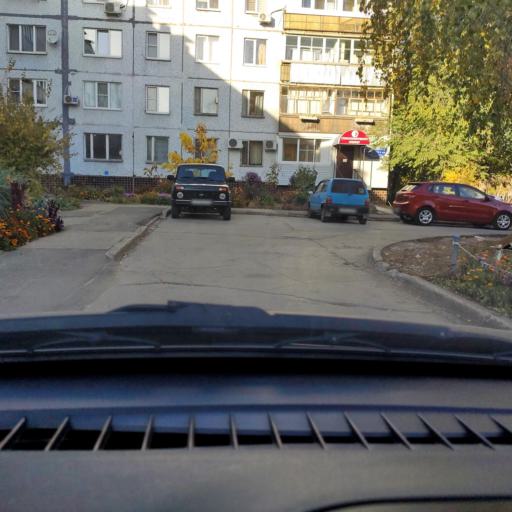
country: RU
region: Samara
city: Tol'yatti
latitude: 53.5333
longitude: 49.2636
